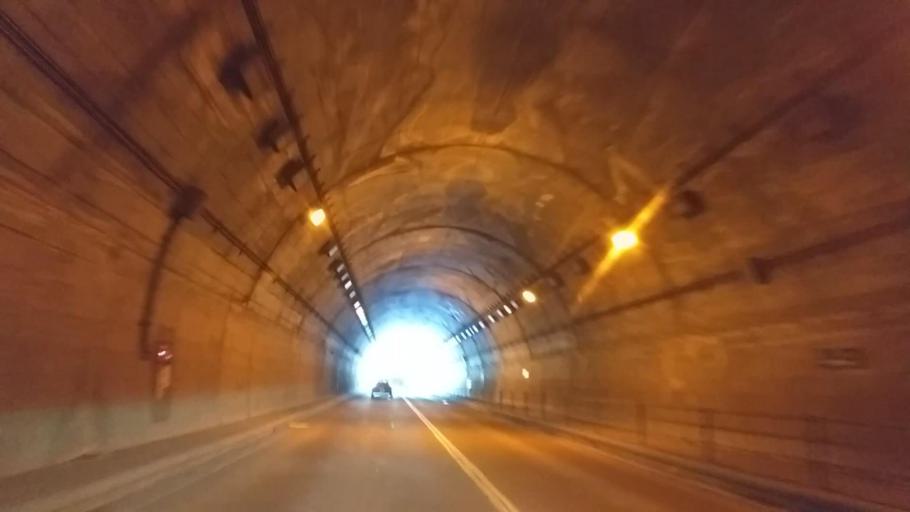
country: JP
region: Chiba
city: Kawaguchi
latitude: 35.1277
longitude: 140.1618
